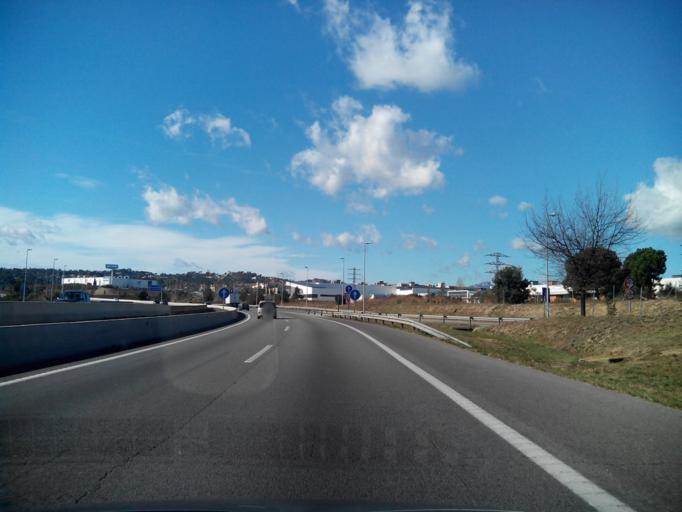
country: ES
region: Catalonia
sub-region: Provincia de Barcelona
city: Terrassa
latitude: 41.5446
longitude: 2.0344
